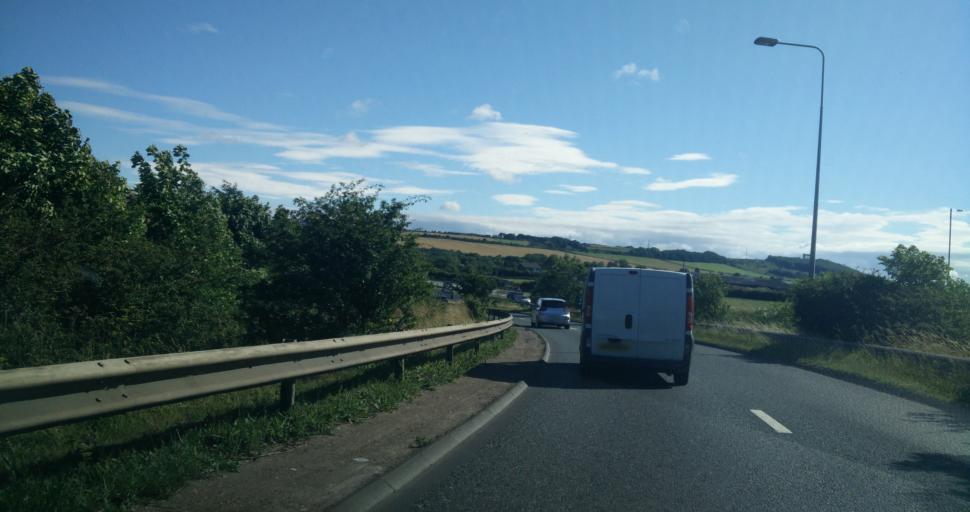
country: GB
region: England
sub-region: South Tyneside
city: The Boldons
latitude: 54.9086
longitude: -1.4601
